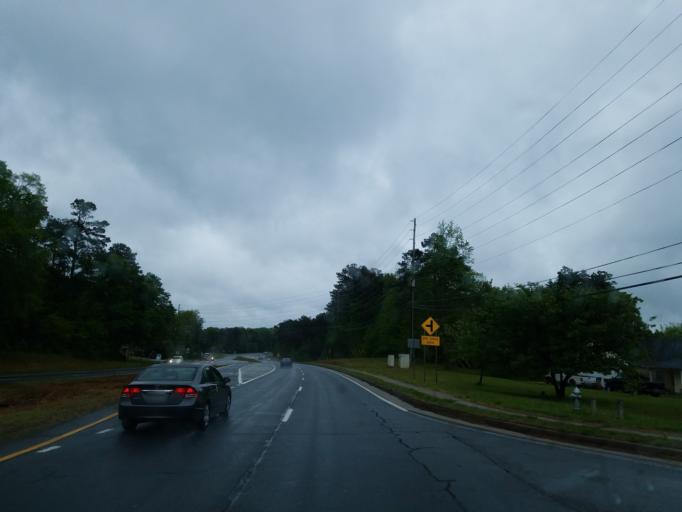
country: US
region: Georgia
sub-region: Cobb County
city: Kennesaw
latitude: 34.0892
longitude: -84.6044
